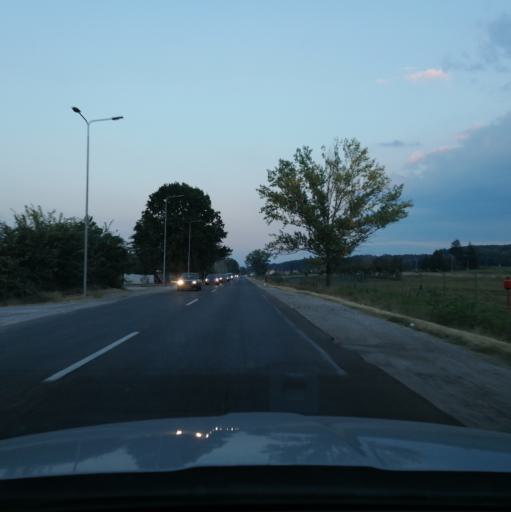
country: RS
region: Central Serbia
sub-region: Raski Okrug
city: Kraljevo
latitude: 43.7044
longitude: 20.7088
